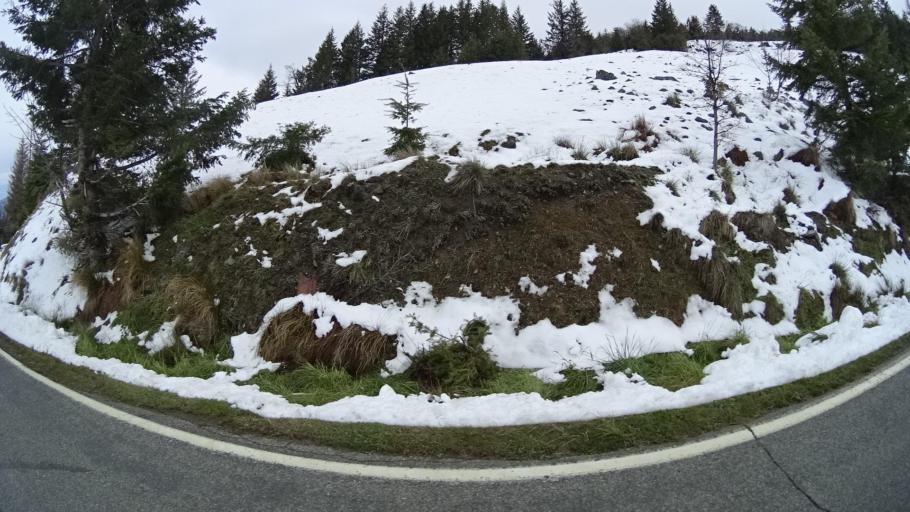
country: US
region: California
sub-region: Humboldt County
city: Willow Creek
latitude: 40.8702
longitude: -123.7515
